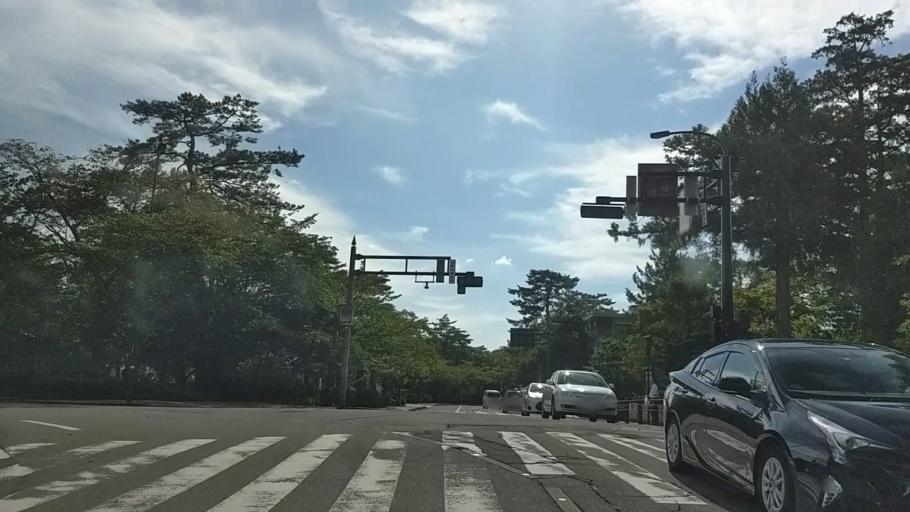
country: JP
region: Ishikawa
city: Kanazawa-shi
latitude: 36.5610
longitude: 136.6648
